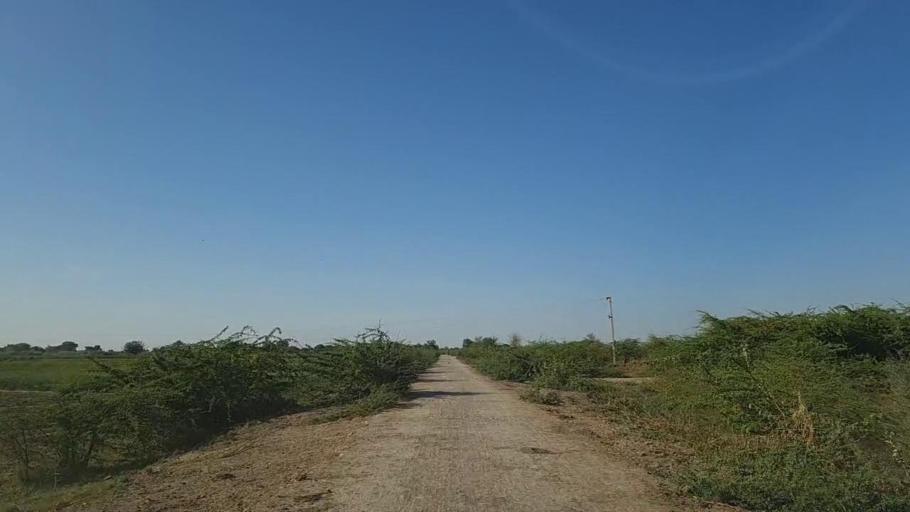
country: PK
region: Sindh
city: Samaro
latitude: 25.2579
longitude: 69.4897
